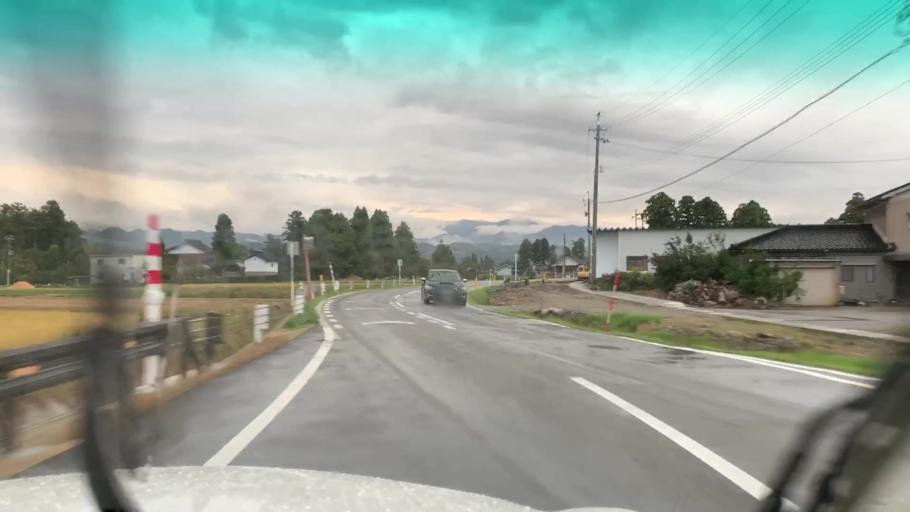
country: JP
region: Toyama
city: Kamiichi
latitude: 36.6460
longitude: 137.3281
